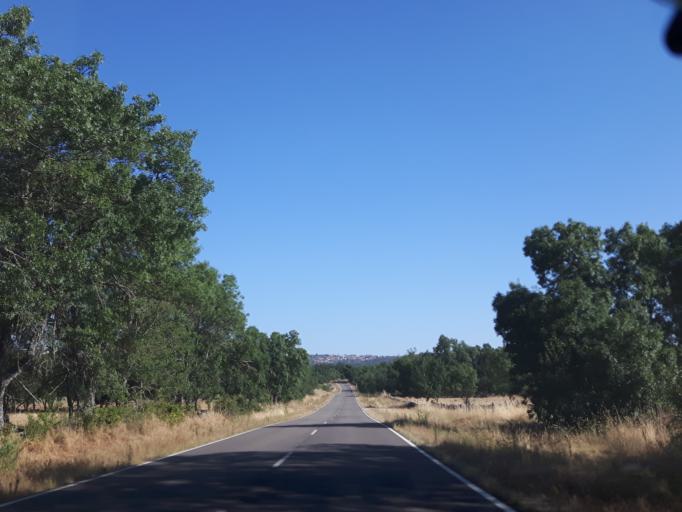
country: ES
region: Castille and Leon
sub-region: Provincia de Salamanca
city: Valdehijaderos
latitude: 40.4225
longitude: -5.8206
